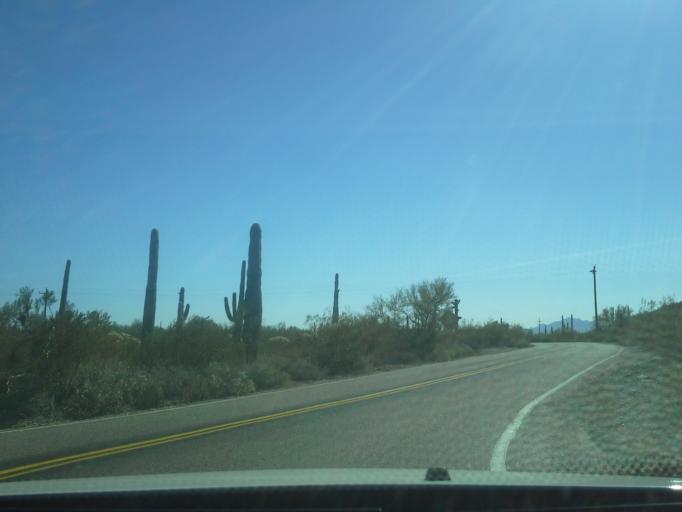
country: MX
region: Sonora
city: Sonoyta
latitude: 31.9557
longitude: -112.8038
